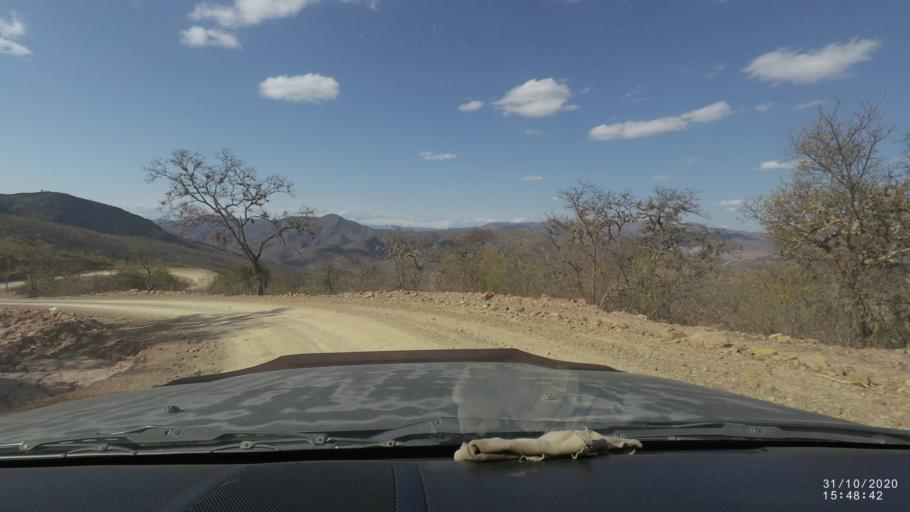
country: BO
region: Chuquisaca
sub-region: Provincia Zudanez
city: Mojocoya
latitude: -18.3106
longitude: -64.7099
